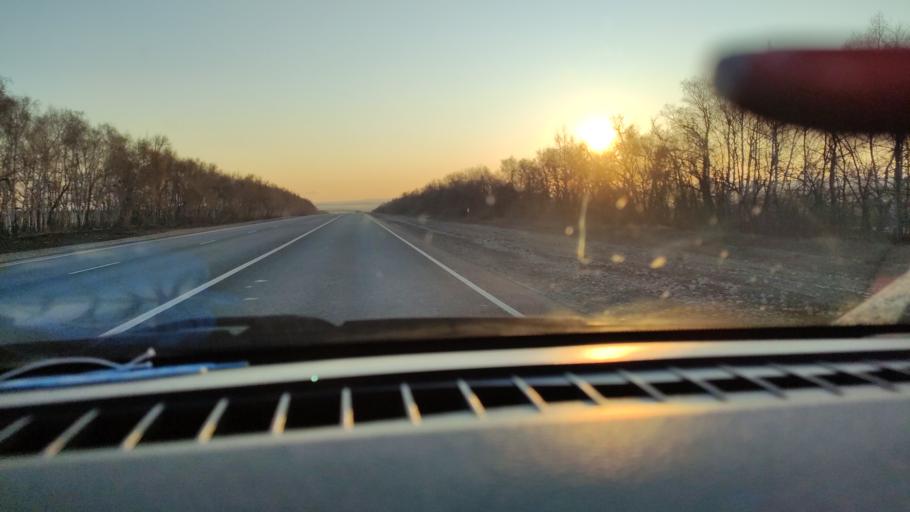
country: RU
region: Saratov
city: Yelshanka
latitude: 51.8988
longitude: 46.5372
